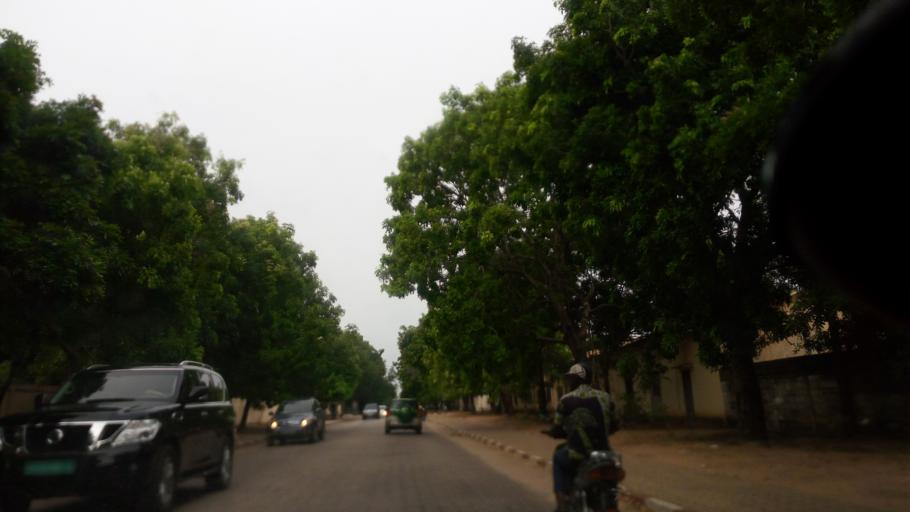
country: BJ
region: Littoral
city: Cotonou
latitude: 6.3564
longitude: 2.4112
